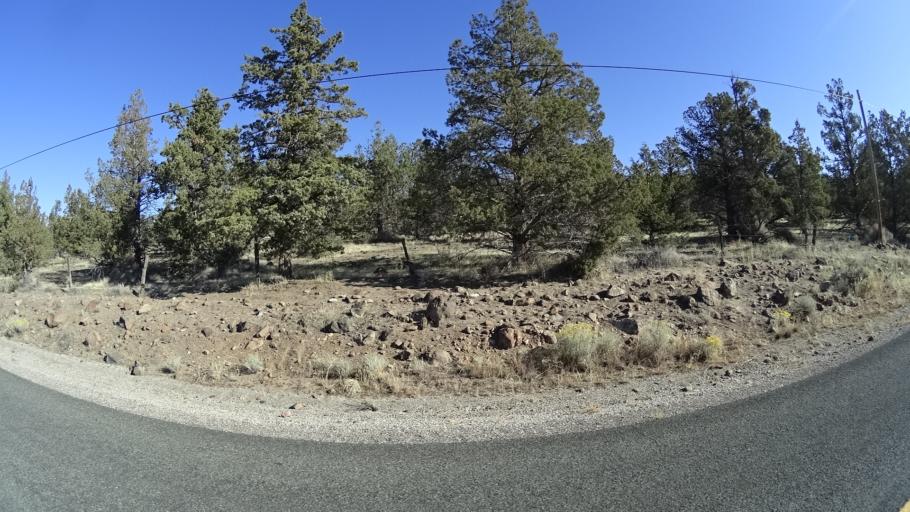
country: US
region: California
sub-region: Siskiyou County
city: Weed
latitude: 41.6292
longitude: -122.3330
